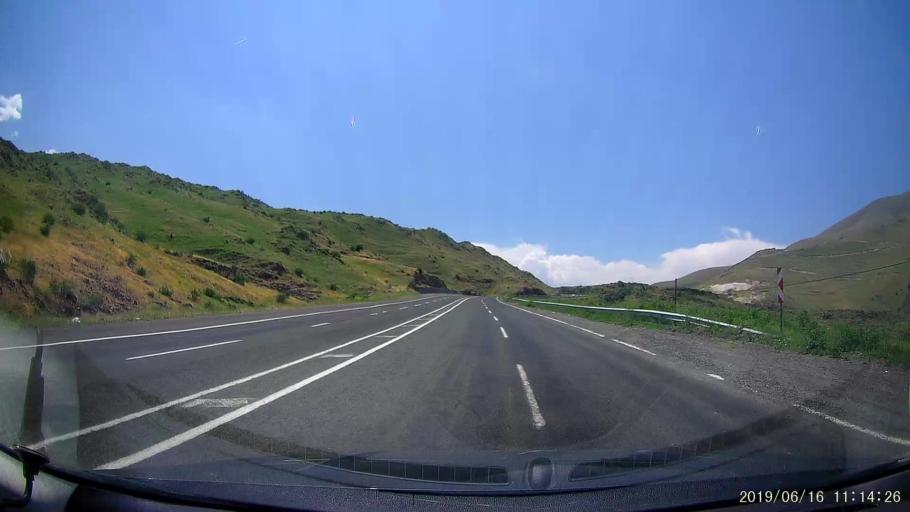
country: TR
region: Igdir
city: Igdir
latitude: 39.7788
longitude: 44.1422
